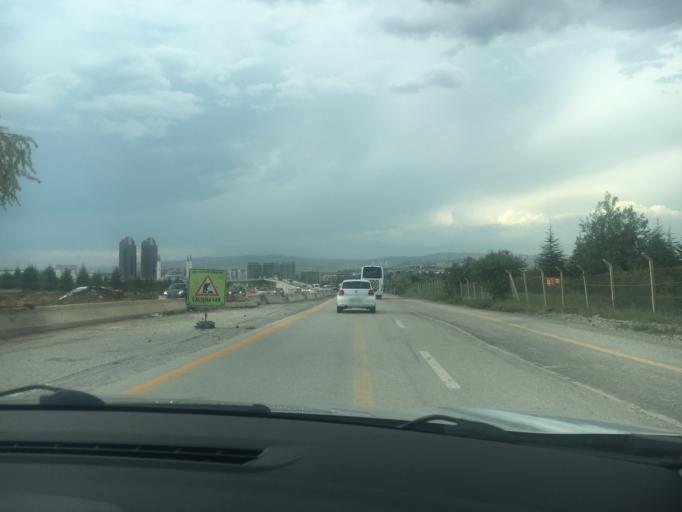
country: TR
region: Ankara
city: Batikent
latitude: 39.8961
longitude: 32.7668
